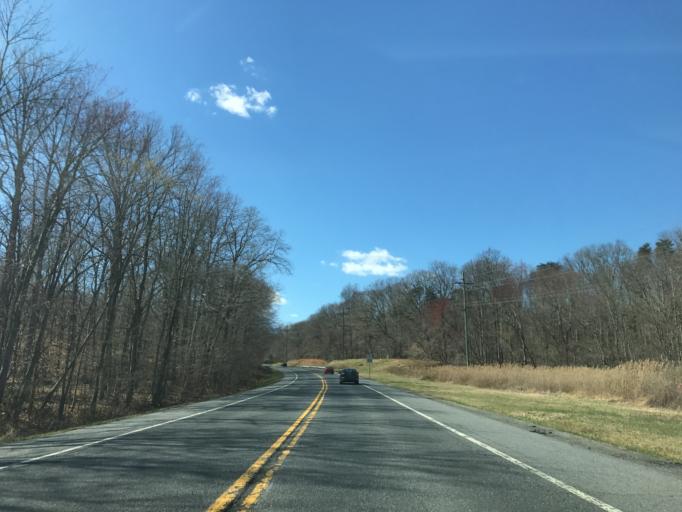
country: US
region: Maryland
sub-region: Queen Anne's County
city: Kingstown
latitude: 39.2649
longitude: -75.8680
